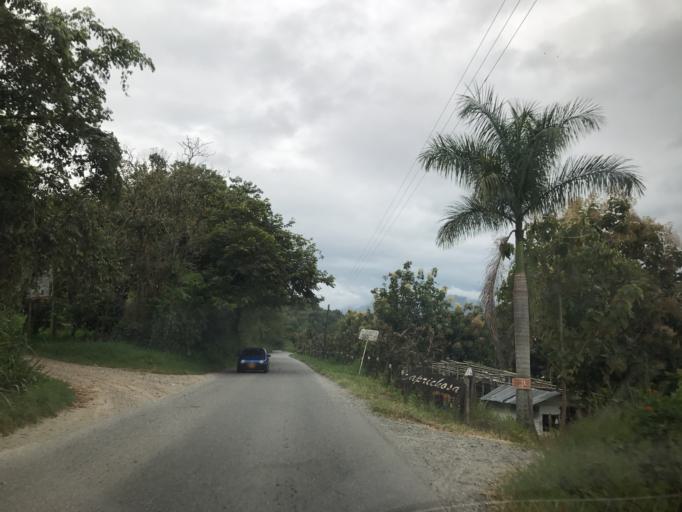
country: CO
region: Quindio
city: Genova
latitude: 4.3318
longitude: -75.7895
